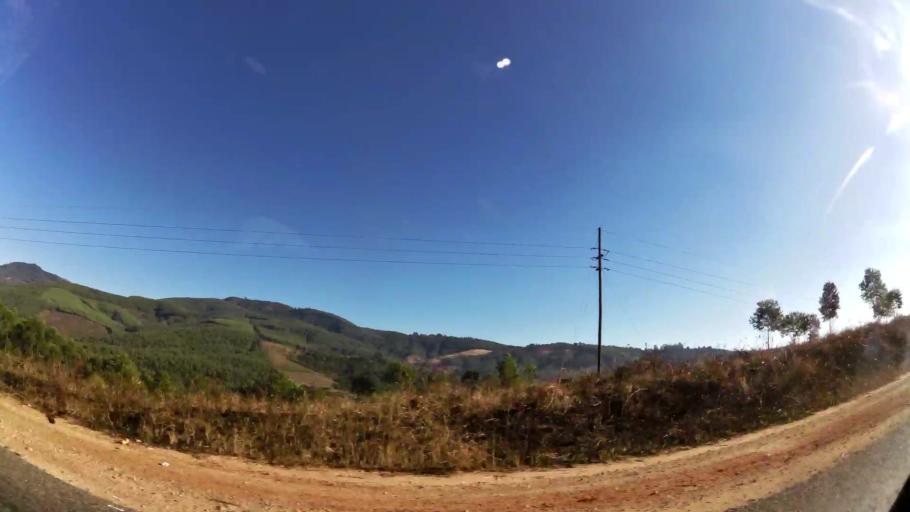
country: ZA
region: Limpopo
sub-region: Mopani District Municipality
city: Tzaneen
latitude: -23.8731
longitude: 30.0946
